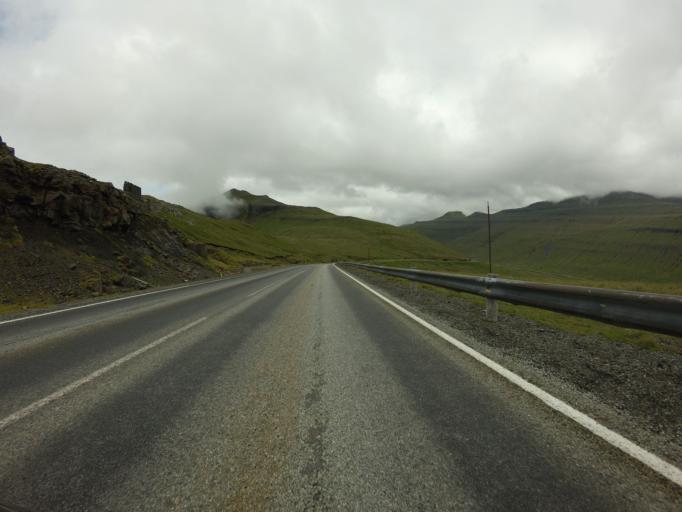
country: FO
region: Streymoy
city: Kollafjordhur
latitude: 62.1027
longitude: -6.9796
